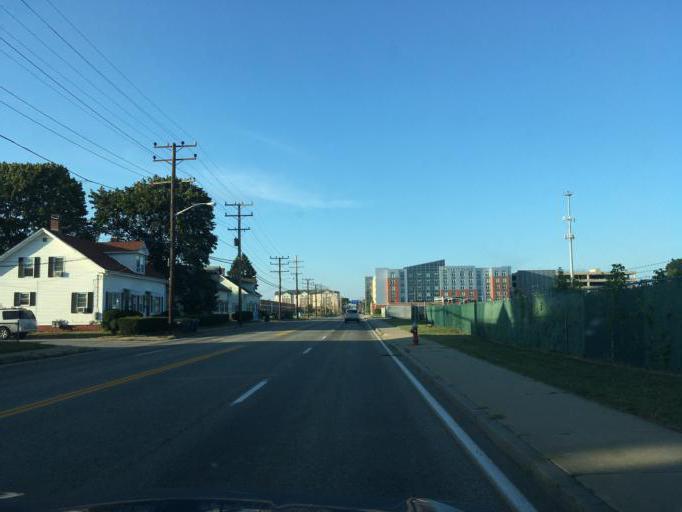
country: US
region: Rhode Island
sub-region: Kent County
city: Warwick
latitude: 41.7240
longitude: -71.4447
